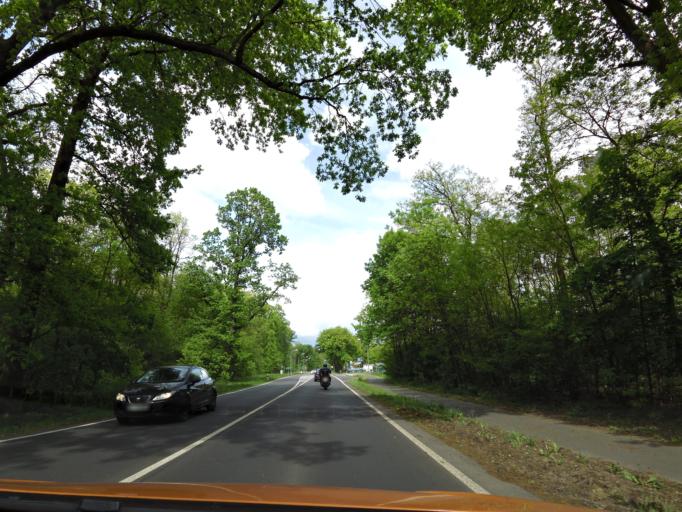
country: DE
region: Brandenburg
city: Michendorf
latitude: 52.2879
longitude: 13.0168
